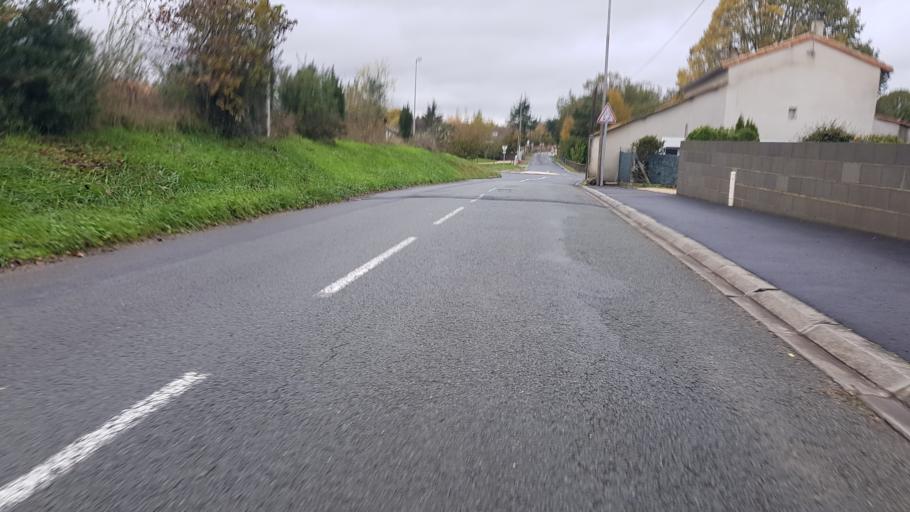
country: FR
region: Poitou-Charentes
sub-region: Departement de la Vienne
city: Avanton
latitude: 46.6567
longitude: 0.3372
